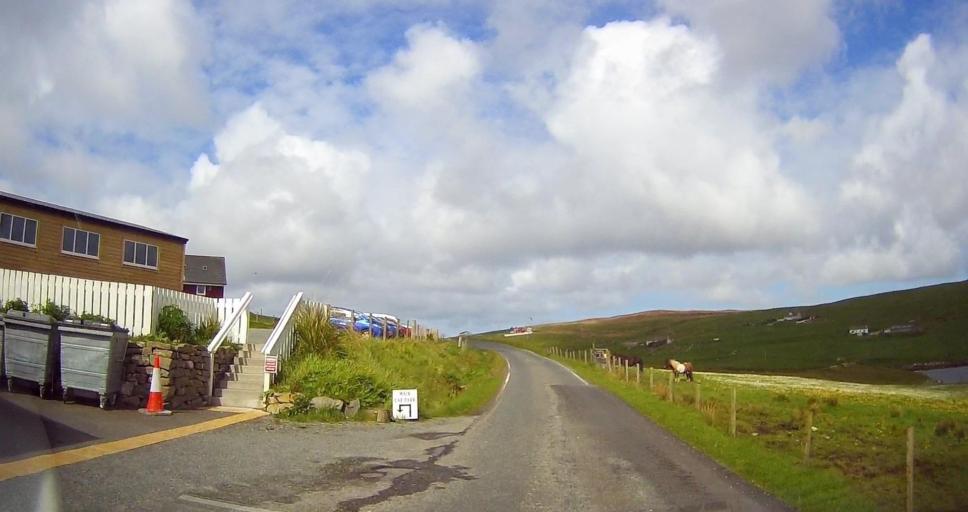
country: GB
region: Scotland
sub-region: Shetland Islands
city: Lerwick
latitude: 60.3021
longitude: -1.3464
